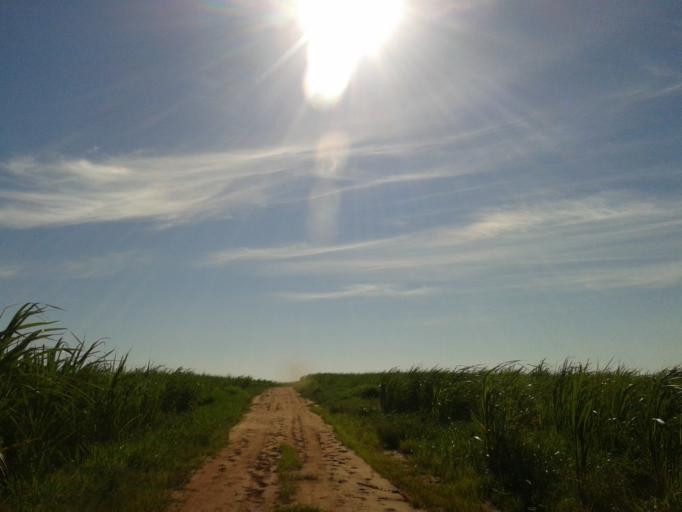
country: BR
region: Minas Gerais
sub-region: Santa Vitoria
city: Santa Vitoria
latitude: -19.1254
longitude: -50.0063
